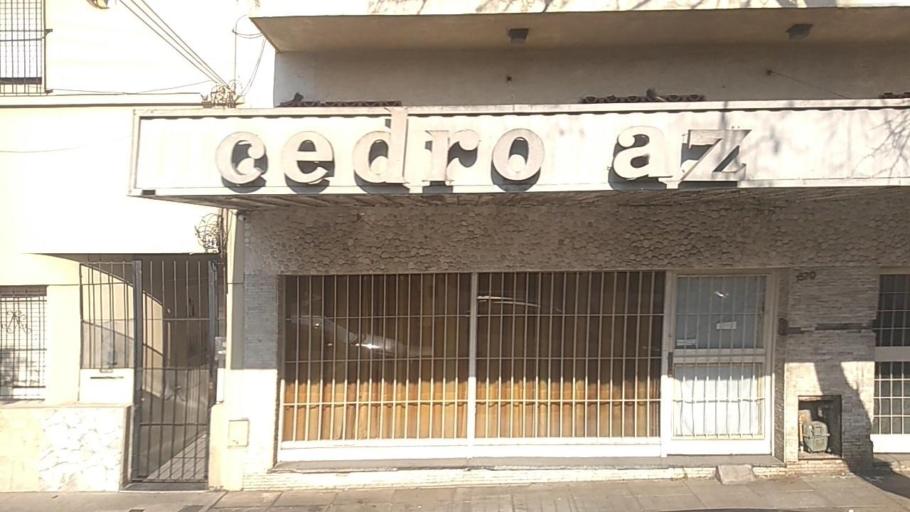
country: AR
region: Buenos Aires F.D.
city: Villa Santa Rita
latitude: -34.6237
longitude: -58.5041
